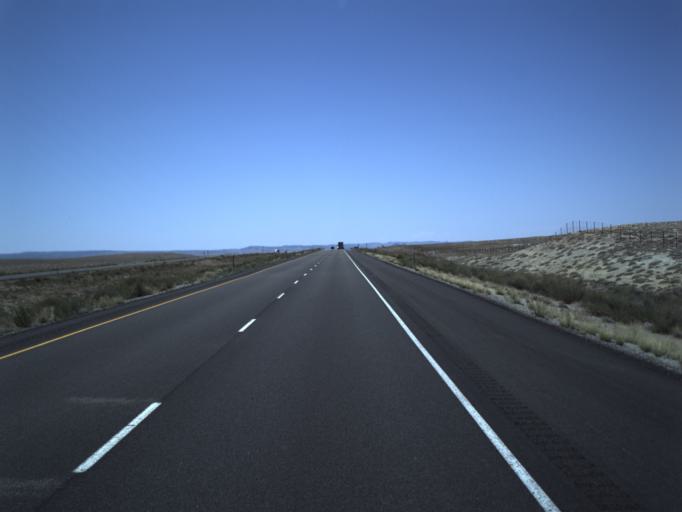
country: US
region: Colorado
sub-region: Mesa County
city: Loma
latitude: 39.0570
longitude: -109.2586
